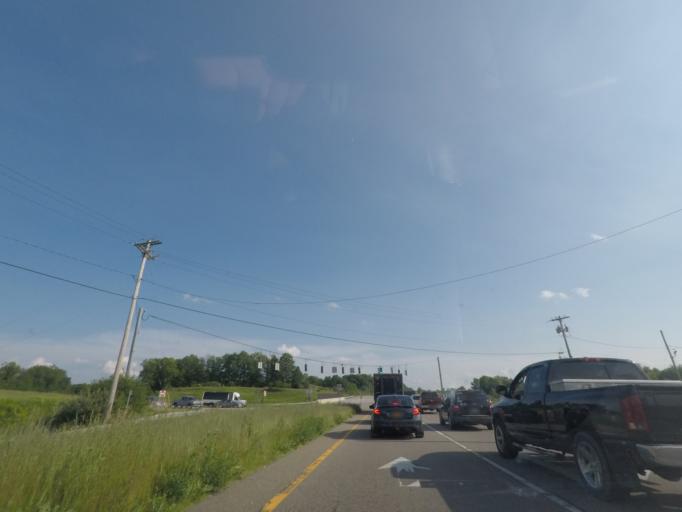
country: US
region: New York
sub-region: Orange County
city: Orange Lake
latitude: 41.5137
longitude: -74.1304
